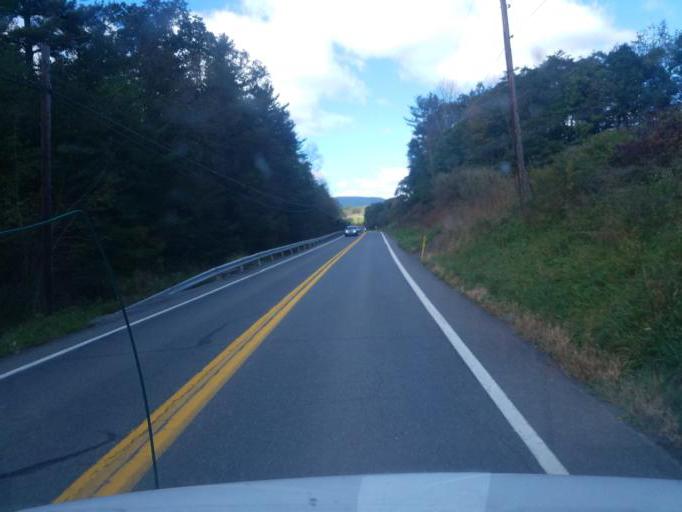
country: US
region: Pennsylvania
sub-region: Fulton County
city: McConnellsburg
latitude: 39.9895
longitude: -78.0697
